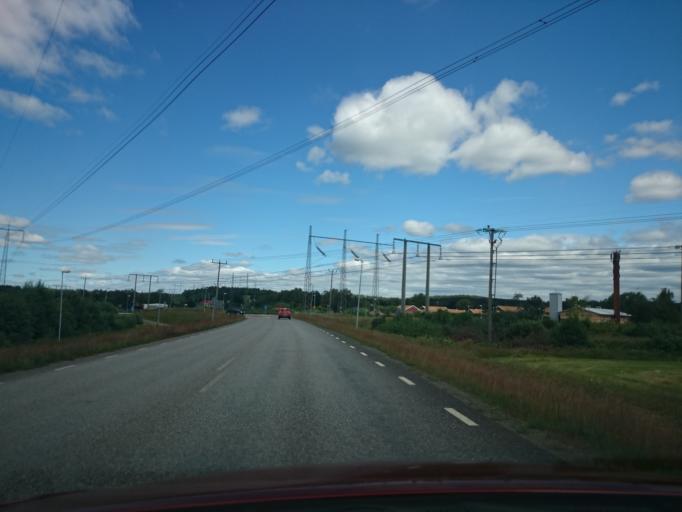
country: SE
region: Vaestra Goetaland
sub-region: Lerums Kommun
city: Grabo
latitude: 57.8335
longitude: 12.2918
